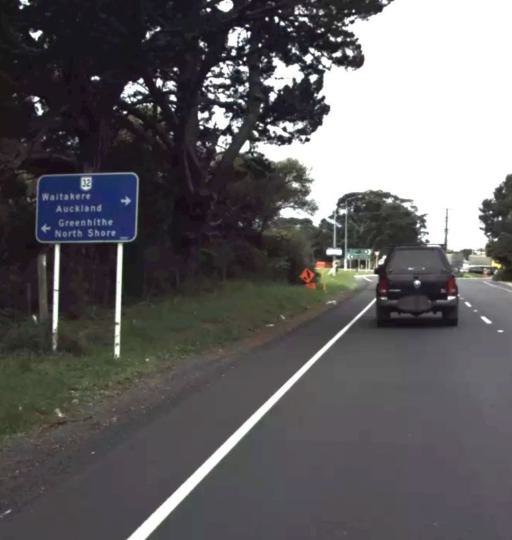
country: NZ
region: Auckland
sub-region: Auckland
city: Rosebank
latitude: -36.7999
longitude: 174.6422
